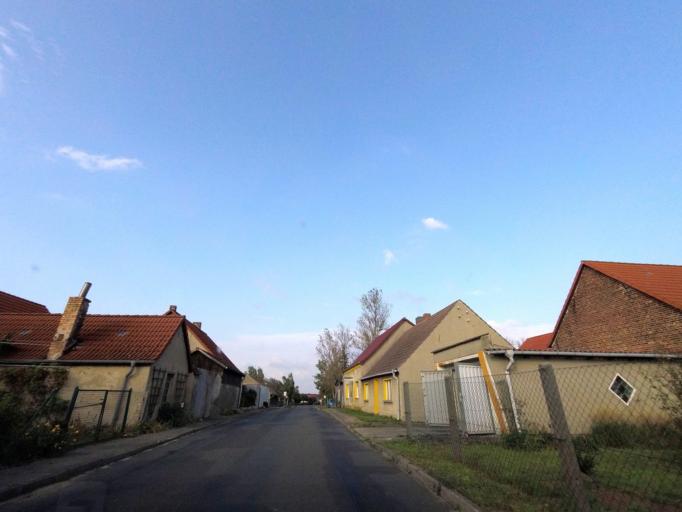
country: DE
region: Brandenburg
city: Niemegk
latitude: 52.1262
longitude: 12.7063
